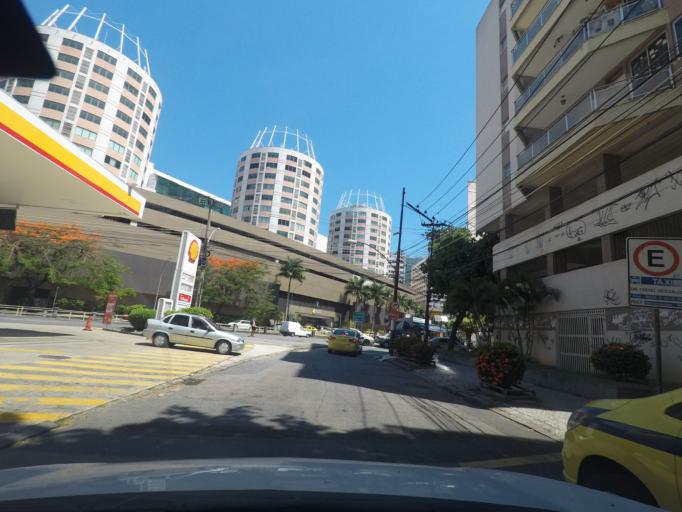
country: BR
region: Rio de Janeiro
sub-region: Rio De Janeiro
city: Rio de Janeiro
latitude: -22.9212
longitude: -43.2360
